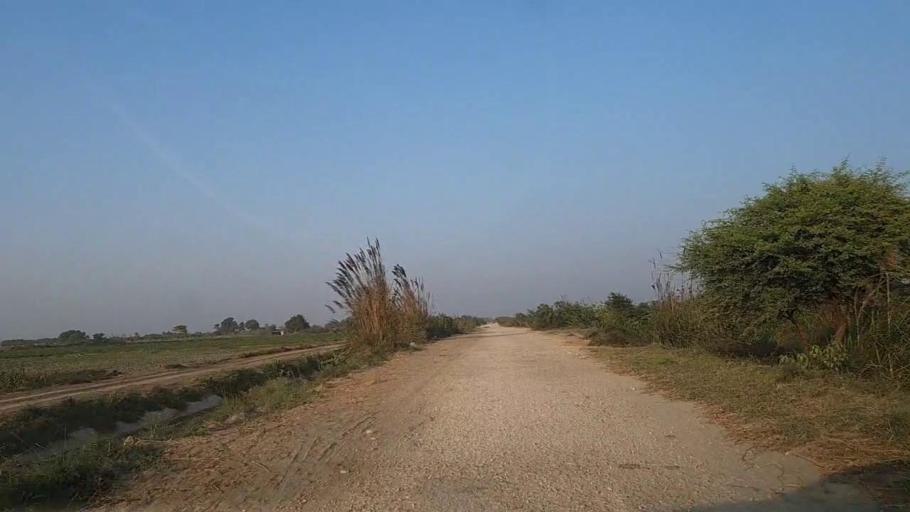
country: PK
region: Sindh
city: Mirpur Sakro
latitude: 24.2811
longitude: 67.6873
